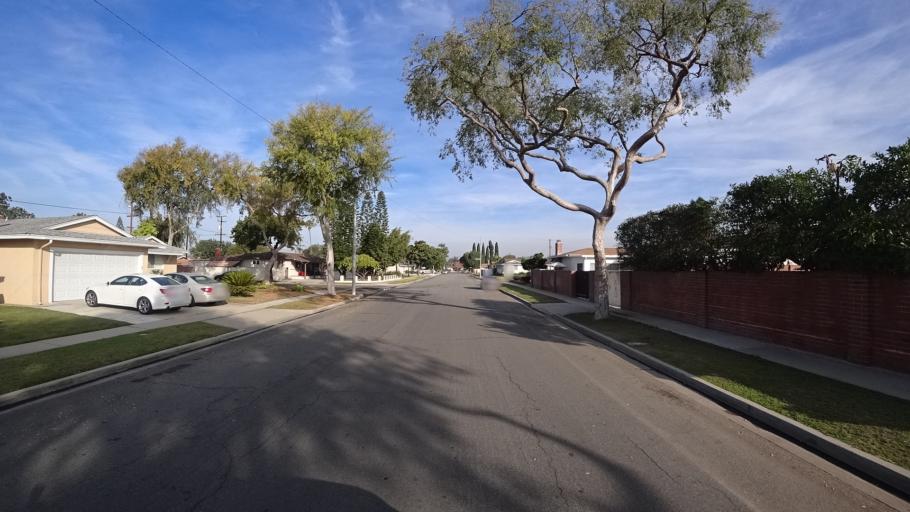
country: US
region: California
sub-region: Orange County
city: Garden Grove
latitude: 33.7925
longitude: -117.9342
